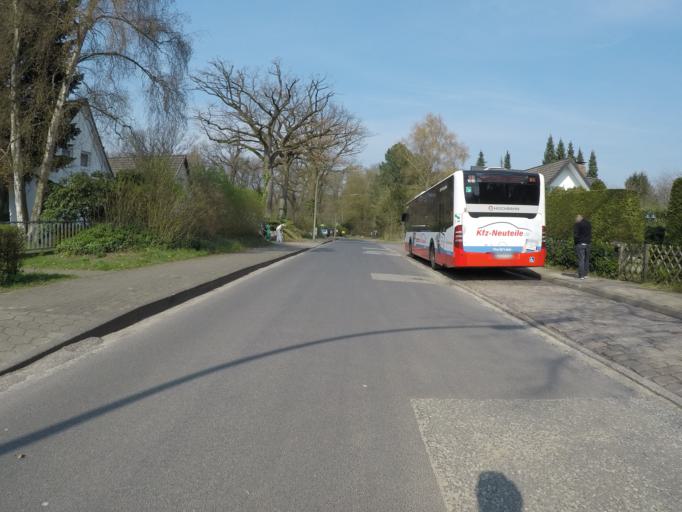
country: DE
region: Hamburg
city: Sasel
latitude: 53.6679
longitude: 10.1062
